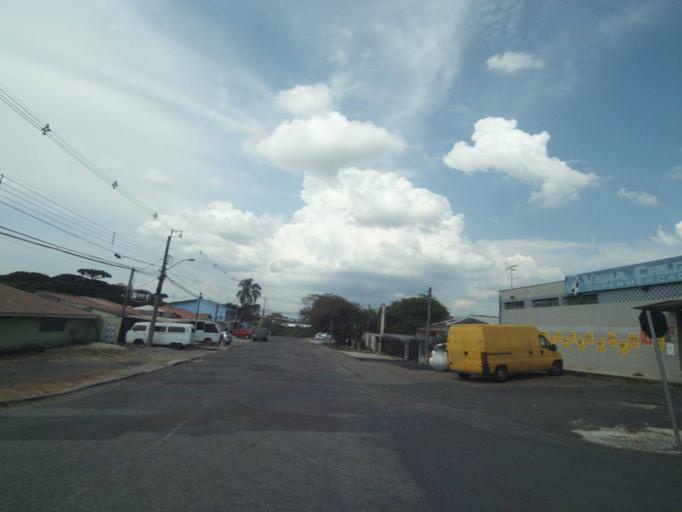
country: BR
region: Parana
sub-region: Pinhais
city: Pinhais
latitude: -25.3986
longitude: -49.1986
